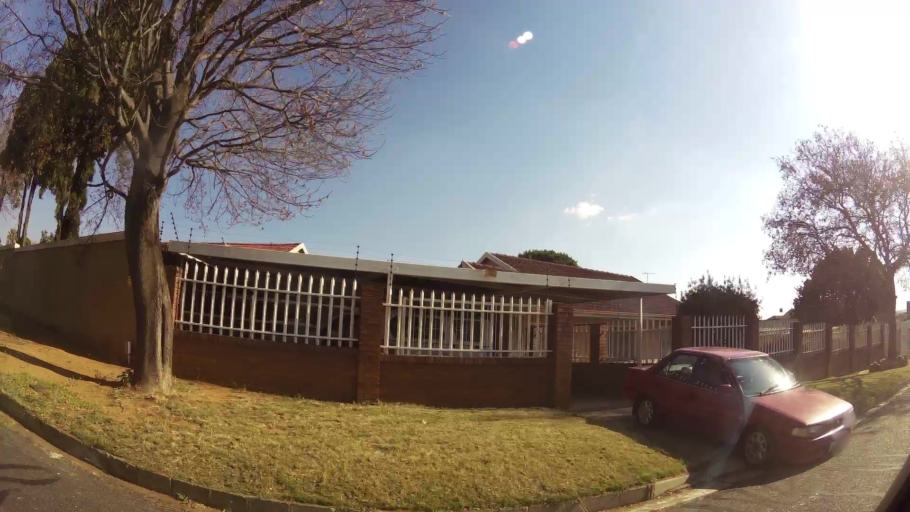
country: ZA
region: Gauteng
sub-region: City of Johannesburg Metropolitan Municipality
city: Johannesburg
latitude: -26.2550
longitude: 27.9961
